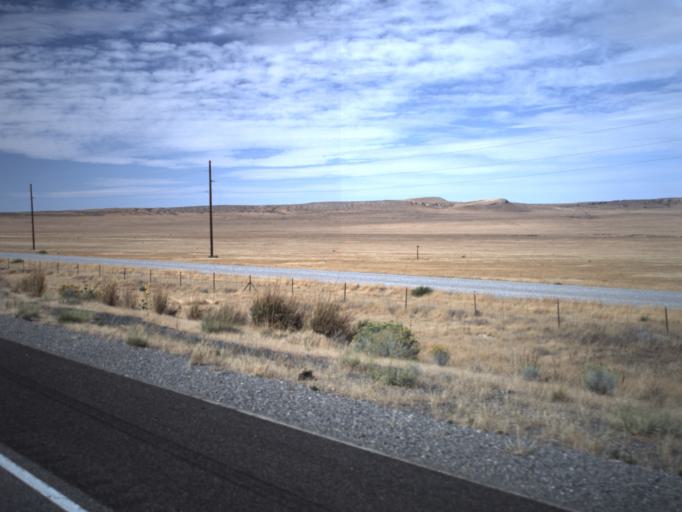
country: US
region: Utah
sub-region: Tooele County
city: Grantsville
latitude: 40.7885
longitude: -112.9583
